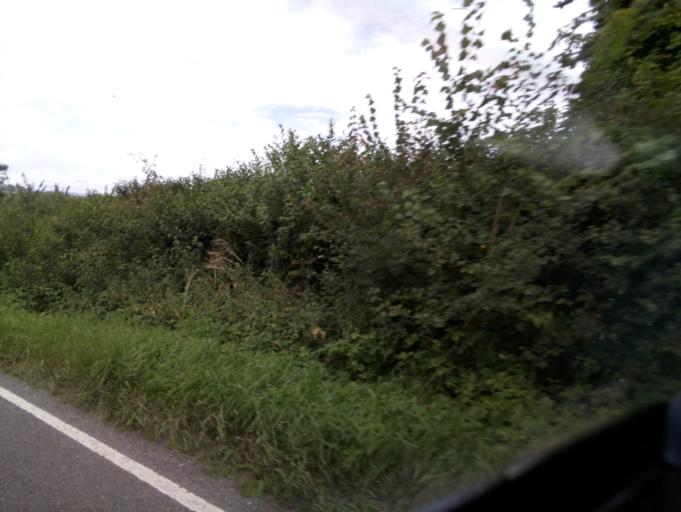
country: GB
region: England
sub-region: Somerset
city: Street
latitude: 51.1186
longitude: -2.7109
